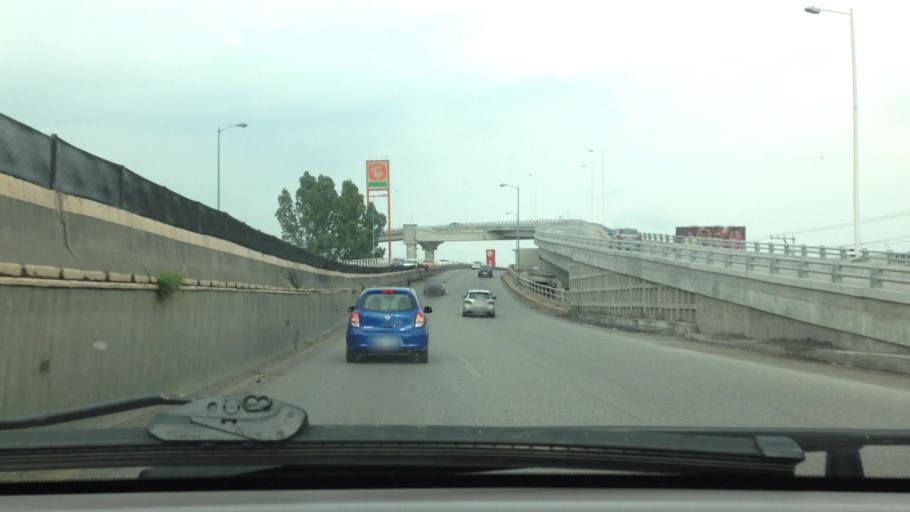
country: MX
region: Morelos
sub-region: Tepoztlan
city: Loma Bonita
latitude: 18.9209
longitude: -99.2017
